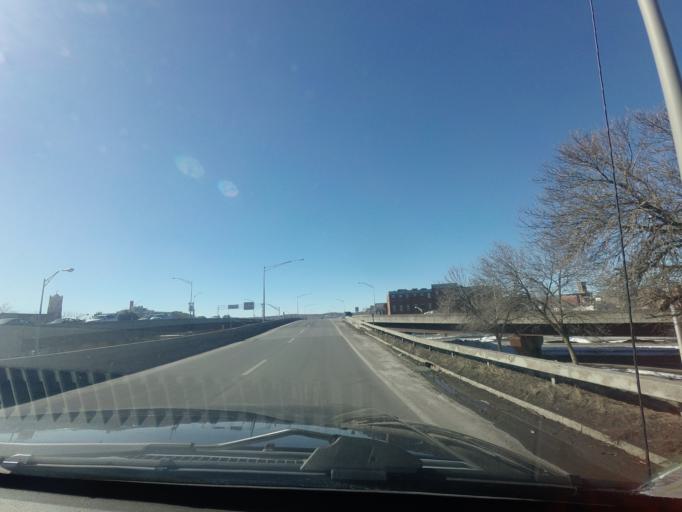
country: US
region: New York
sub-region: Albany County
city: Green Island
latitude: 42.7398
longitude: -73.6823
